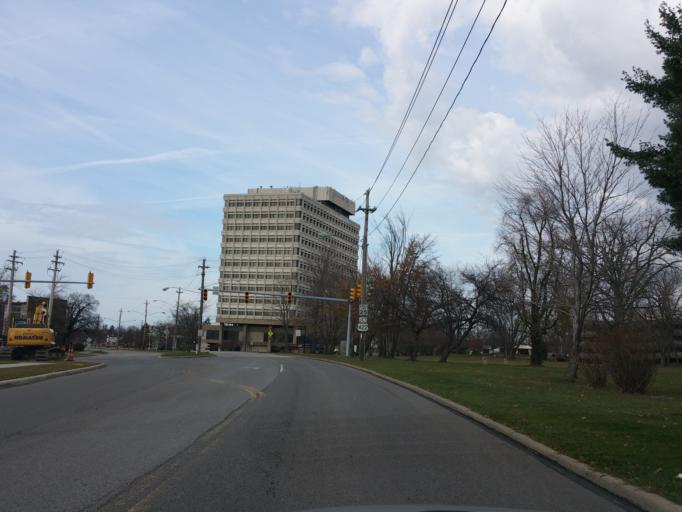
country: US
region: Ohio
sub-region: Cuyahoga County
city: Shaker Heights
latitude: 41.4619
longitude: -81.5333
